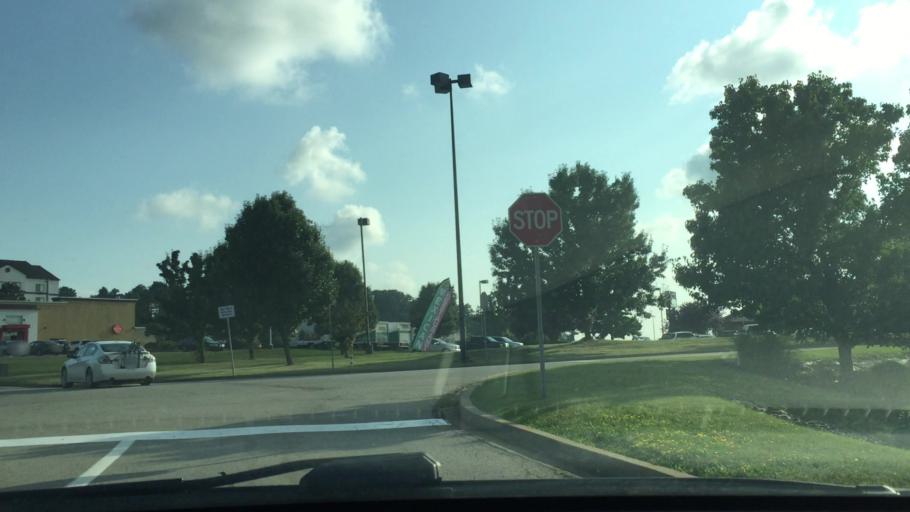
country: US
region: Pennsylvania
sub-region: Washington County
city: East Washington
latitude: 40.1844
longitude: -80.2236
